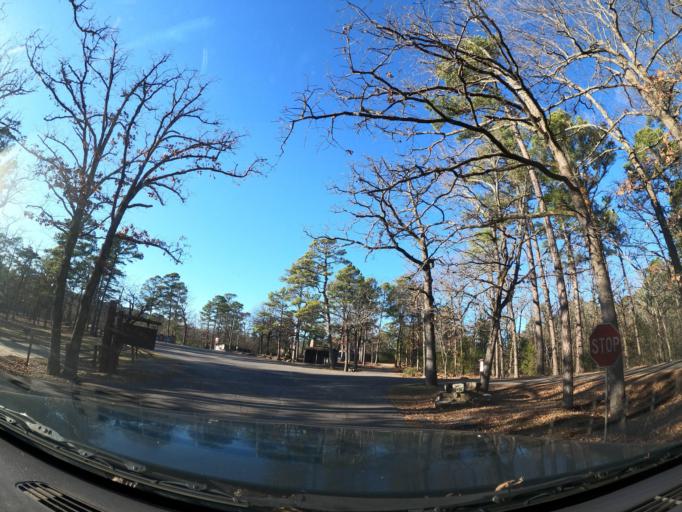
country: US
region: Oklahoma
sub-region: Latimer County
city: Wilburton
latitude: 34.9819
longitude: -95.3536
